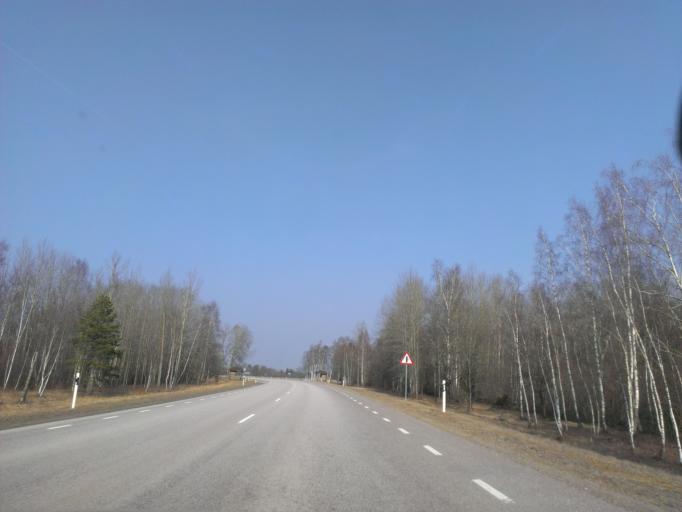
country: EE
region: Saare
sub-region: Orissaare vald
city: Orissaare
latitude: 58.4230
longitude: 22.7888
